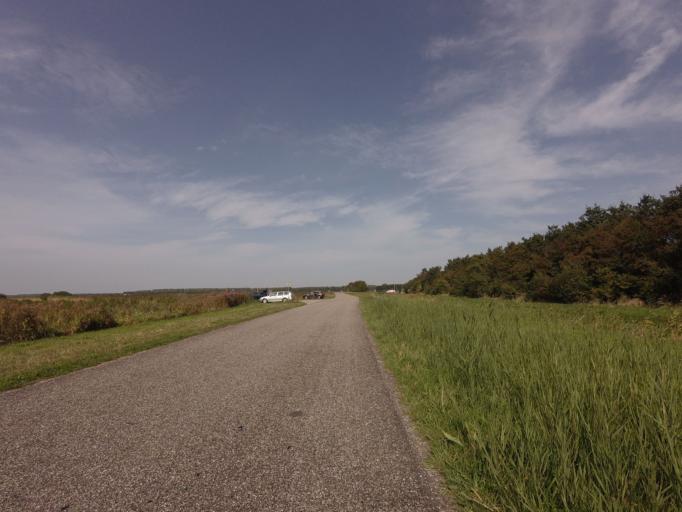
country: NL
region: Groningen
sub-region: Gemeente De Marne
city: Ulrum
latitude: 53.3599
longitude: 6.2610
